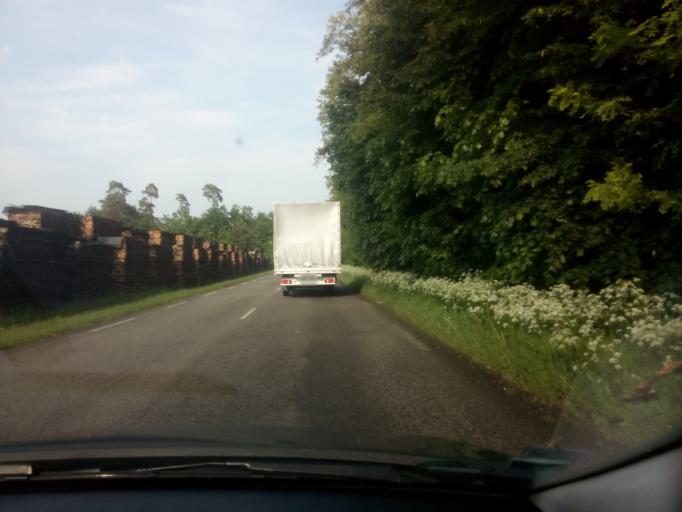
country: FR
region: Alsace
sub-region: Departement du Bas-Rhin
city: Haguenau
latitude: 48.8276
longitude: 7.8142
